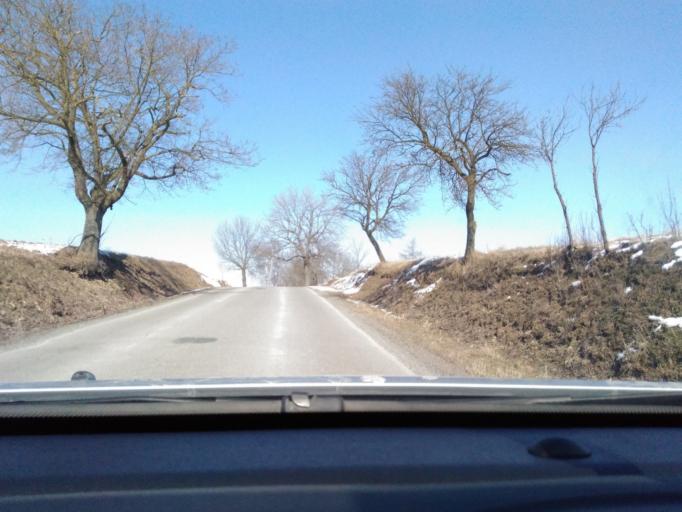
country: CZ
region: Vysocina
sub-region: Okres Zd'ar nad Sazavou
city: Nove Mesto na Morave
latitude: 49.5443
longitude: 16.0608
